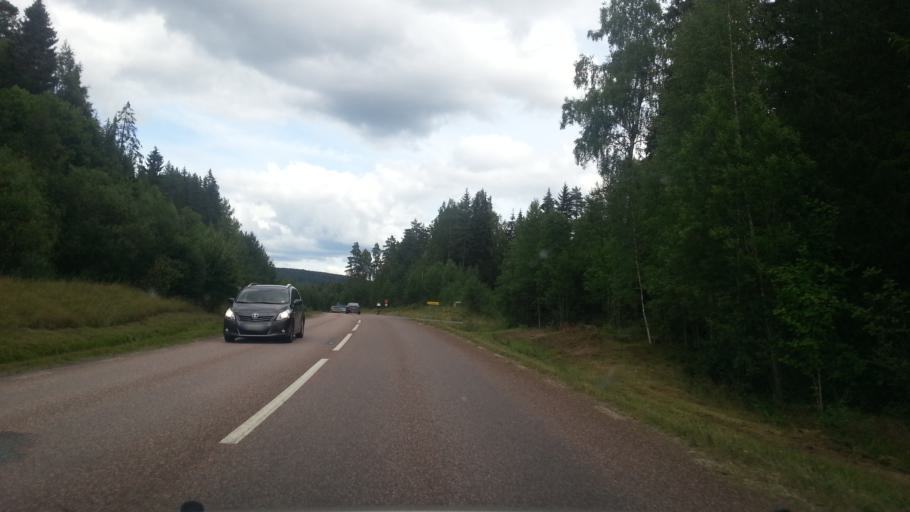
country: SE
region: Dalarna
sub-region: Smedjebackens Kommun
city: Smedjebacken
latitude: 60.1616
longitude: 15.4430
